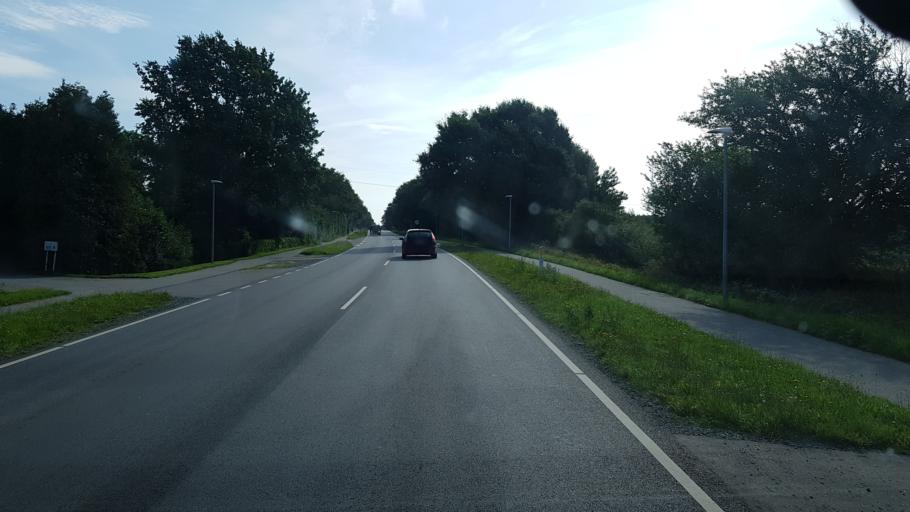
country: DK
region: South Denmark
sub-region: Haderslev Kommune
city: Starup
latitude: 55.2431
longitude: 9.5119
